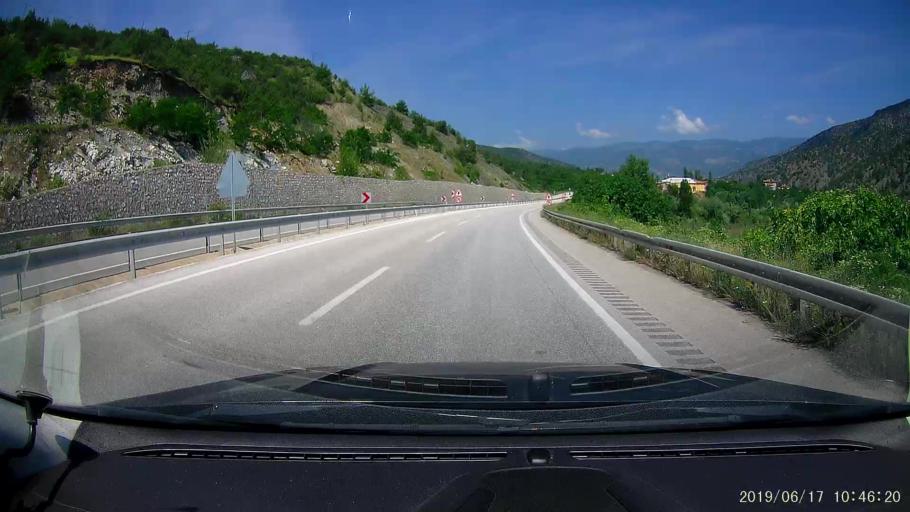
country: TR
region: Corum
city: Hacihamza
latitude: 41.0665
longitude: 34.4642
